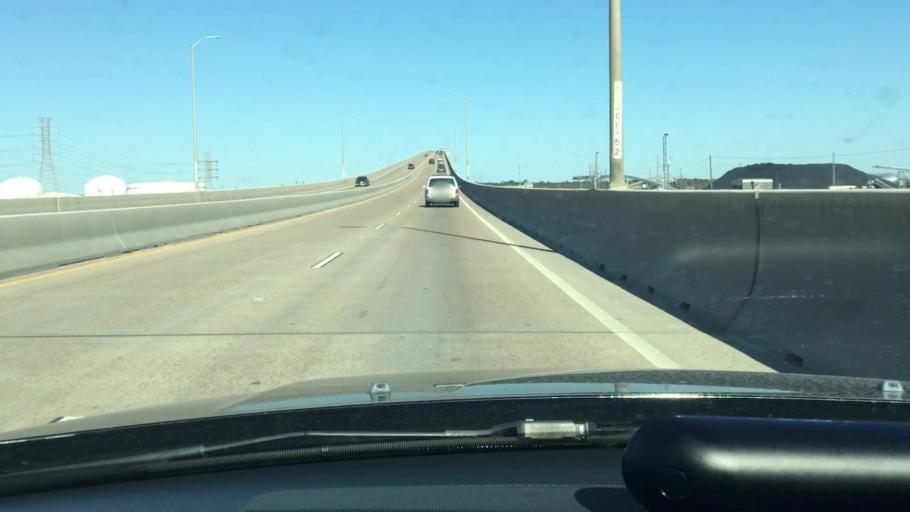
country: US
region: Texas
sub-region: Harris County
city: Deer Park
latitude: 29.7254
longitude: -95.1472
